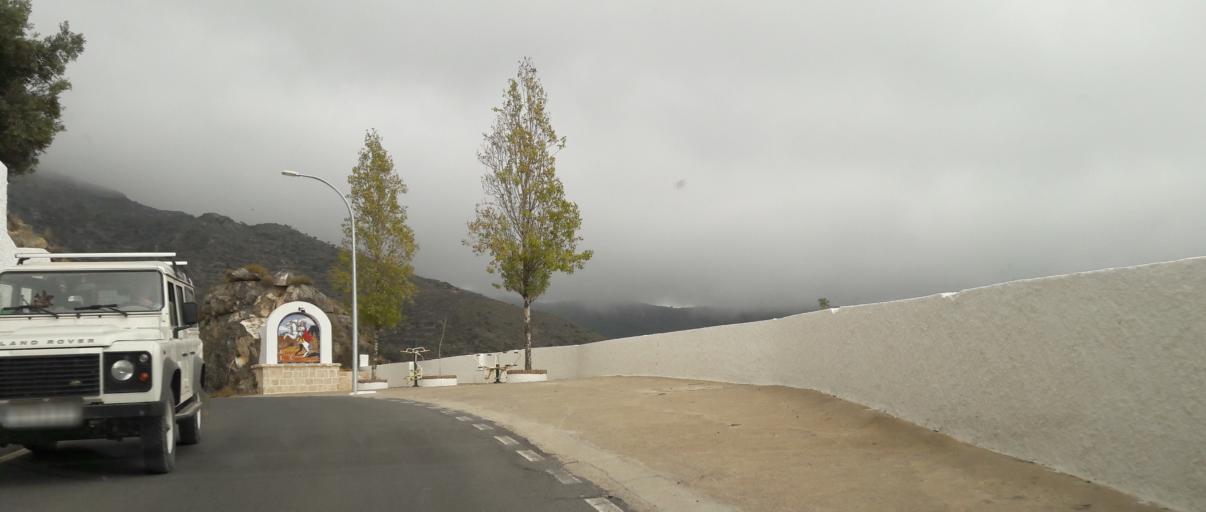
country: ES
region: Andalusia
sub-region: Provincia de Almeria
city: Vicar
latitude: 36.8717
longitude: -2.6532
